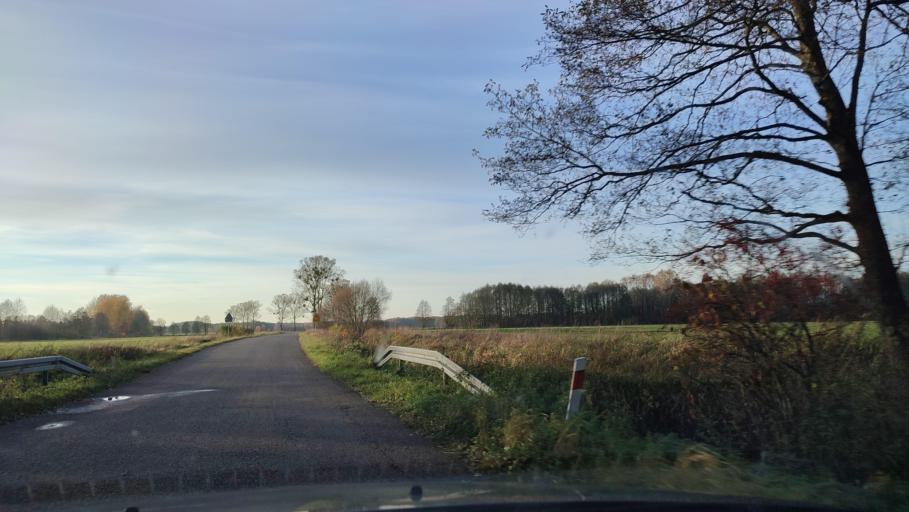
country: PL
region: Masovian Voivodeship
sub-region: Powiat przasnyski
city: Krzynowloga Mala
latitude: 53.3308
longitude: 20.7238
